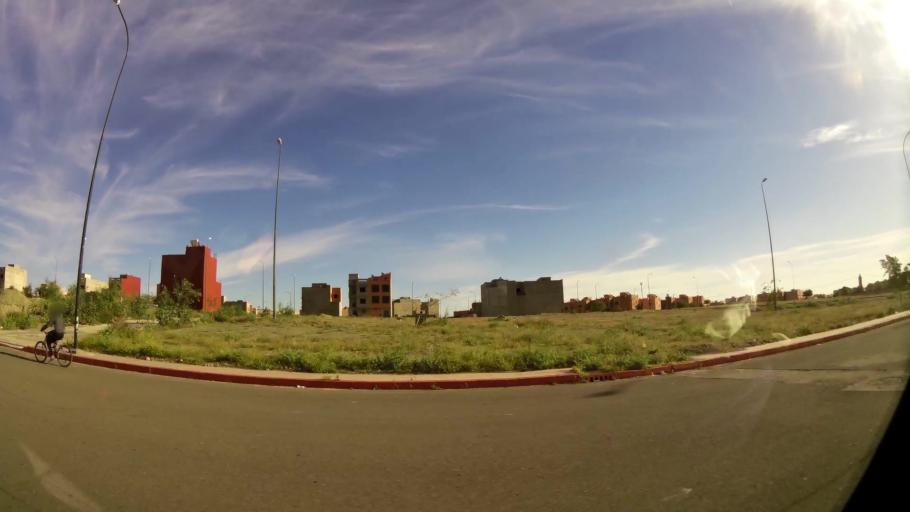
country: MA
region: Marrakech-Tensift-Al Haouz
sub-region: Marrakech
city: Marrakesh
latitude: 31.7541
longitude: -8.1071
